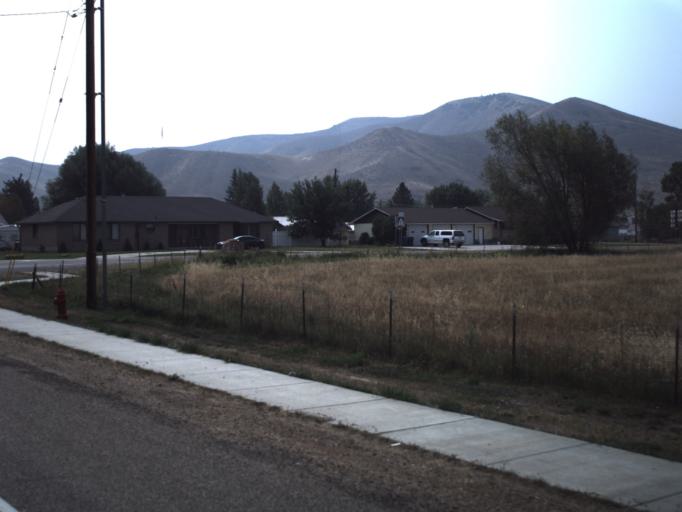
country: US
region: Utah
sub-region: Summit County
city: Coalville
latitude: 41.0210
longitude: -111.5014
